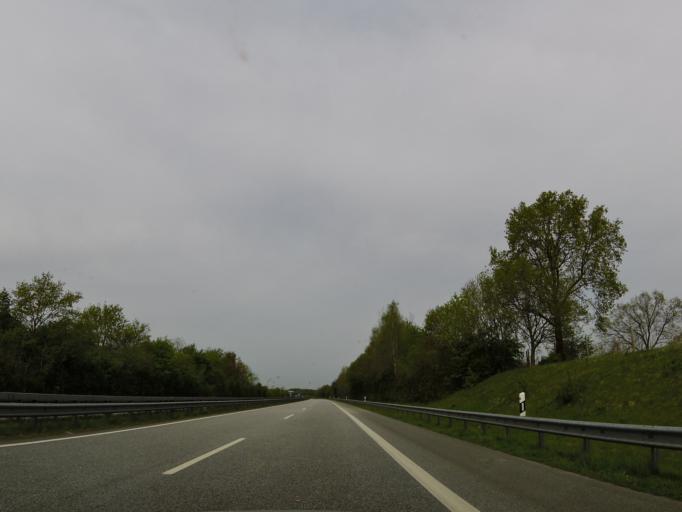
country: DE
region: Schleswig-Holstein
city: Kaisborstel
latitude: 54.0171
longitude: 9.4658
